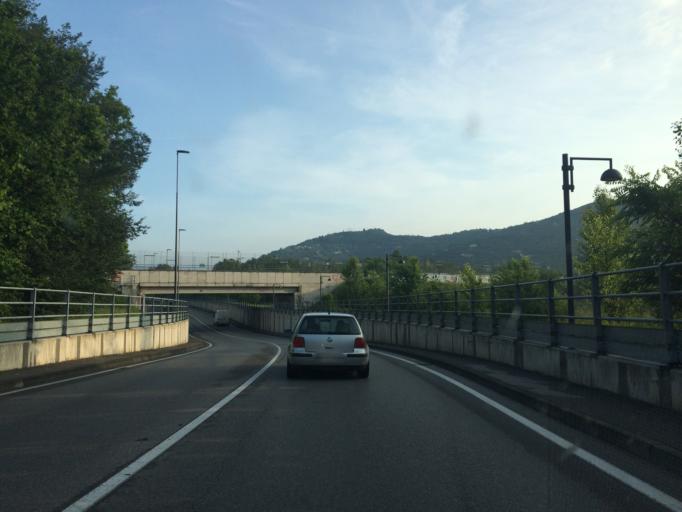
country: IT
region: Lombardy
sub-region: Provincia di Brescia
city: Buffalora-Bettole
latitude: 45.5182
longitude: 10.2484
